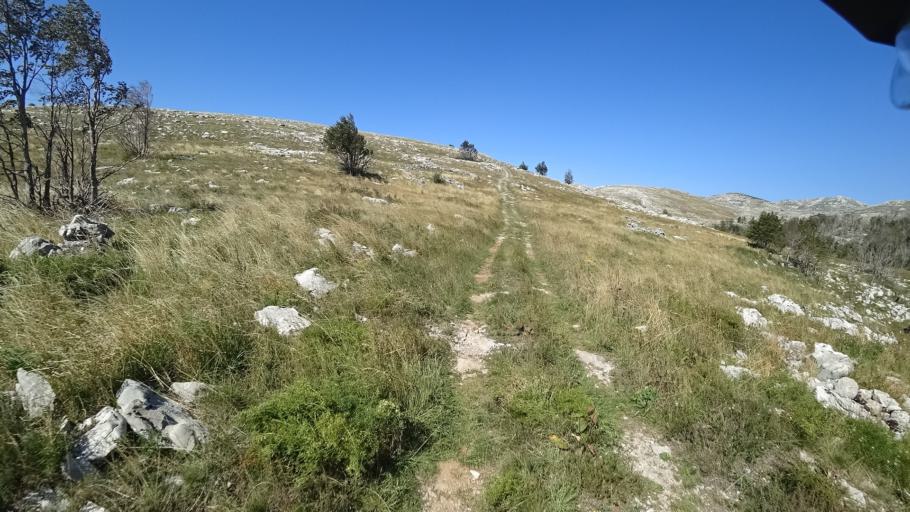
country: HR
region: Splitsko-Dalmatinska
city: Hrvace
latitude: 43.9148
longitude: 16.6100
